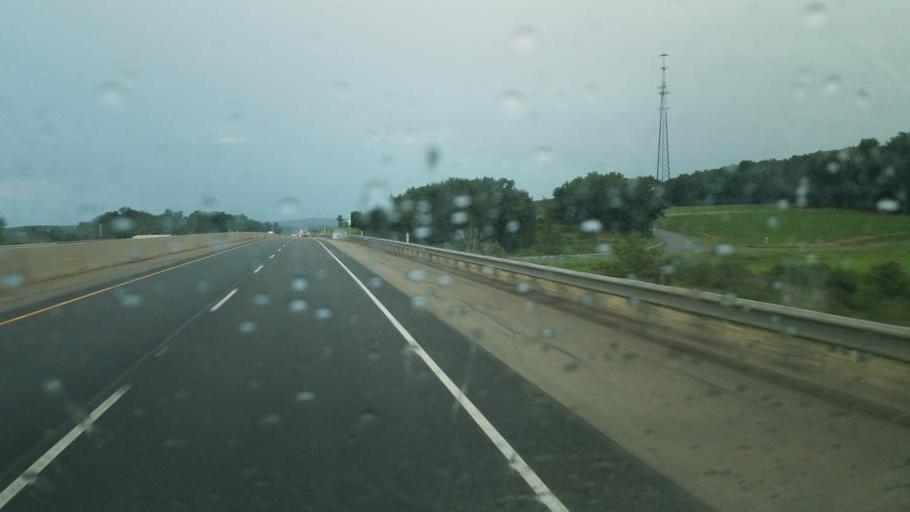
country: US
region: Pennsylvania
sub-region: Somerset County
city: Berlin
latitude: 39.9771
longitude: -78.9320
